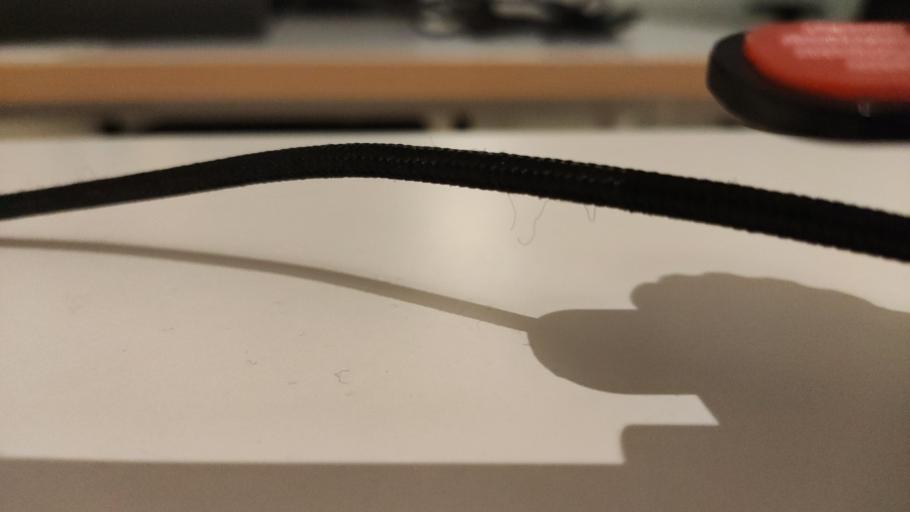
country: RU
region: Moskovskaya
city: Kurovskoye
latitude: 55.5748
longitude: 38.8873
